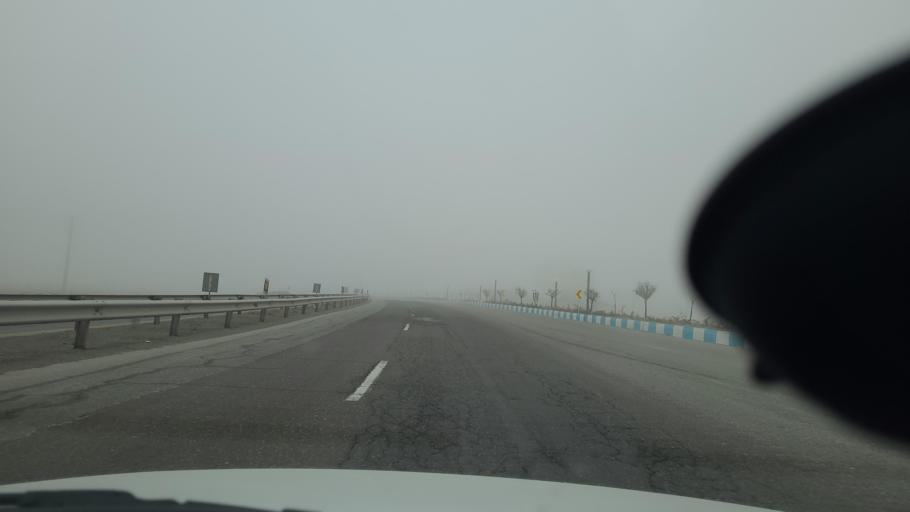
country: IR
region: Razavi Khorasan
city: Fariman
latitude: 35.7799
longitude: 59.7387
